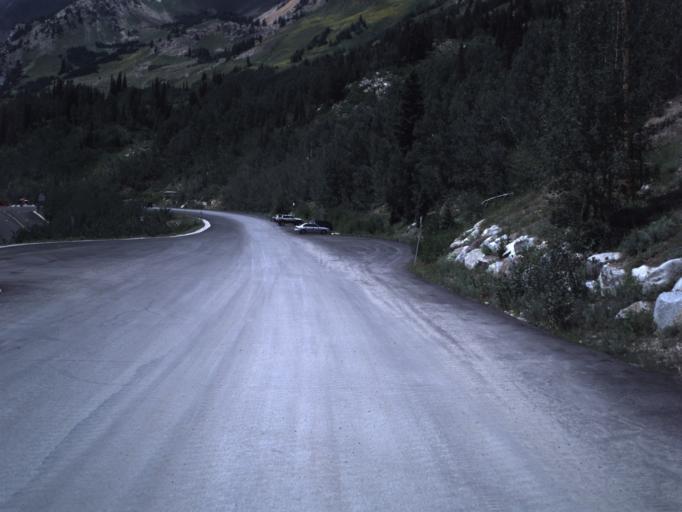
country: US
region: Utah
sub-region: Summit County
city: Snyderville
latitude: 40.5920
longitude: -111.6274
